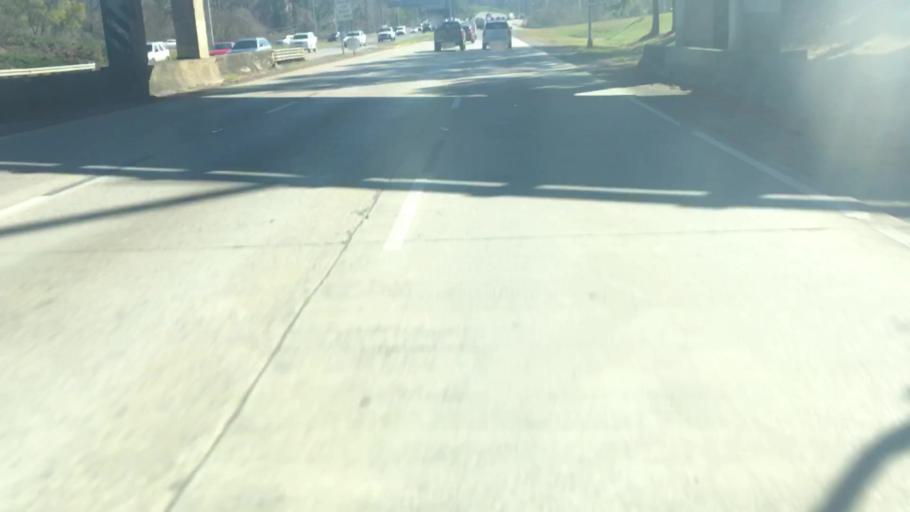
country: US
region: Alabama
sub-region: Jefferson County
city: Homewood
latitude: 33.4824
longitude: -86.7783
